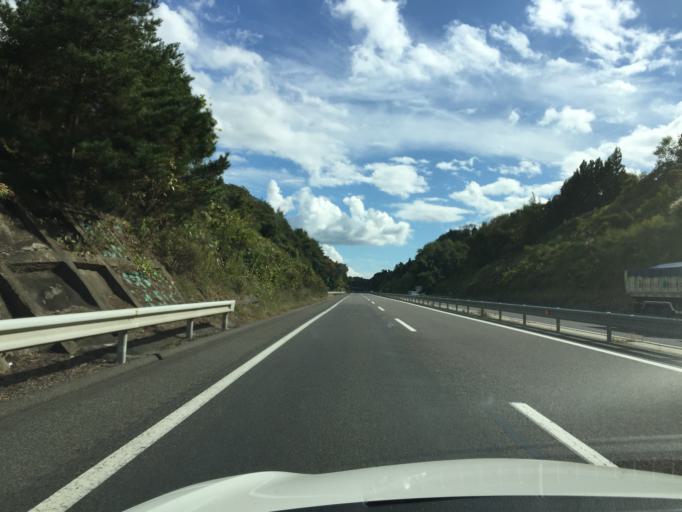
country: JP
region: Fukushima
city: Funehikimachi-funehiki
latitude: 37.4094
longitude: 140.5661
